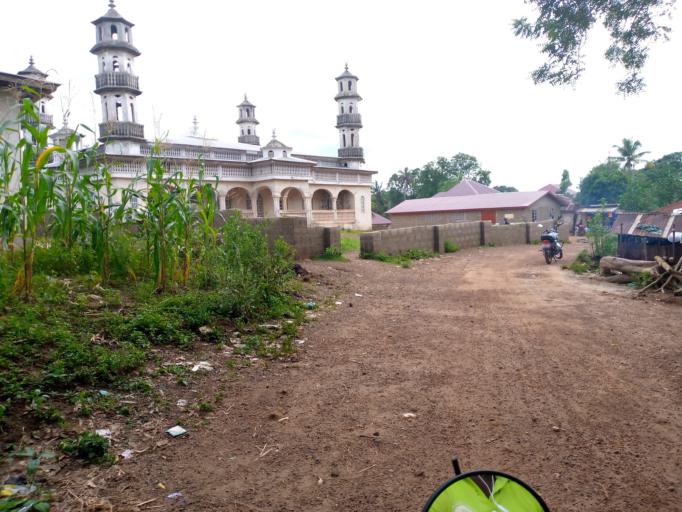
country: SL
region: Northern Province
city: Magburaka
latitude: 8.7228
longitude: -11.9427
